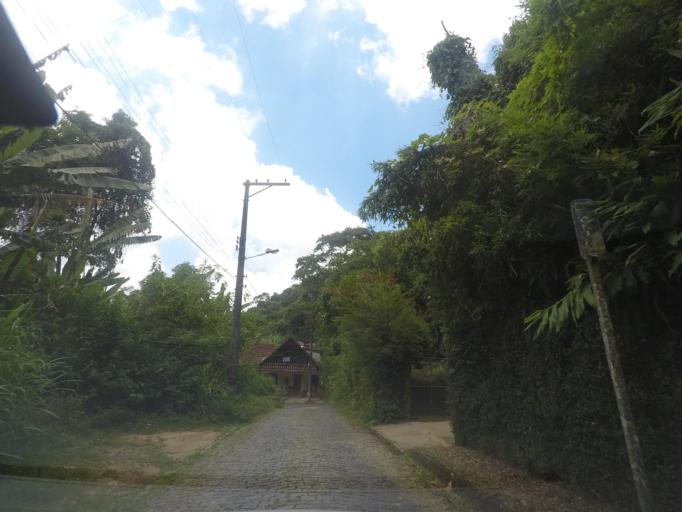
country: BR
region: Rio de Janeiro
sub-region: Petropolis
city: Petropolis
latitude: -22.4979
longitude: -43.1888
